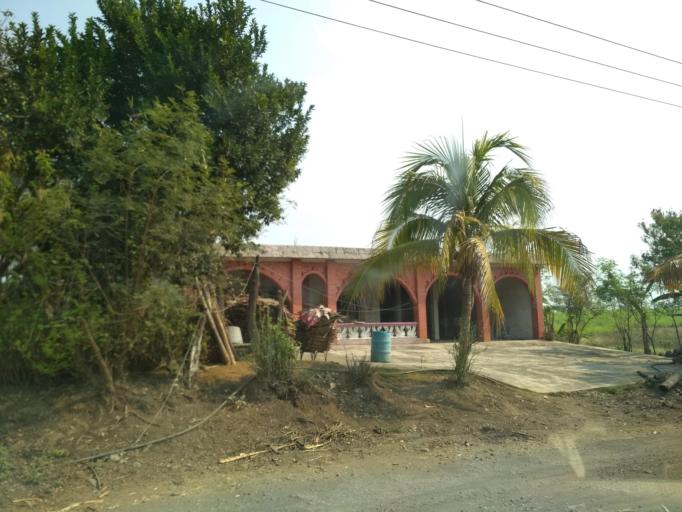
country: MX
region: Oaxaca
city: Acatlan de Perez Figueroa
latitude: 18.6074
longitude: -96.5740
